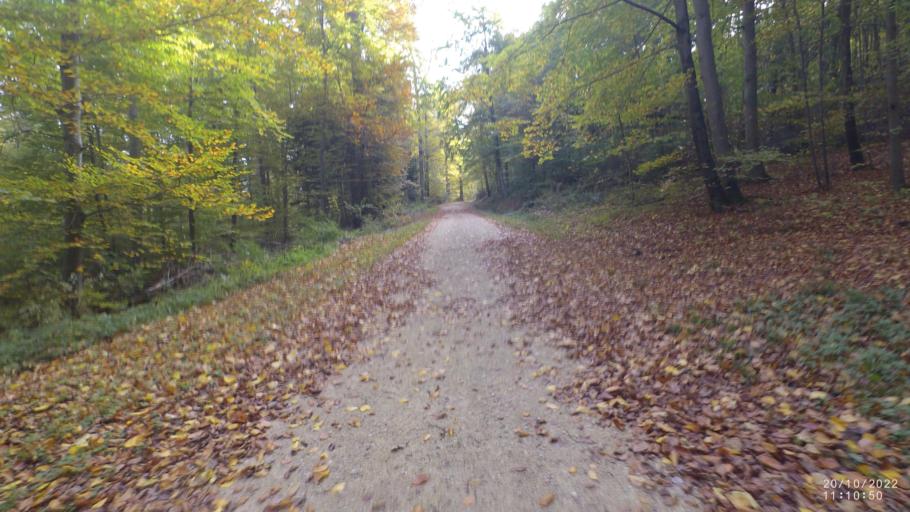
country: DE
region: Baden-Wuerttemberg
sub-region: Regierungsbezirk Stuttgart
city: Boll
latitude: 48.6247
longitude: 9.5913
